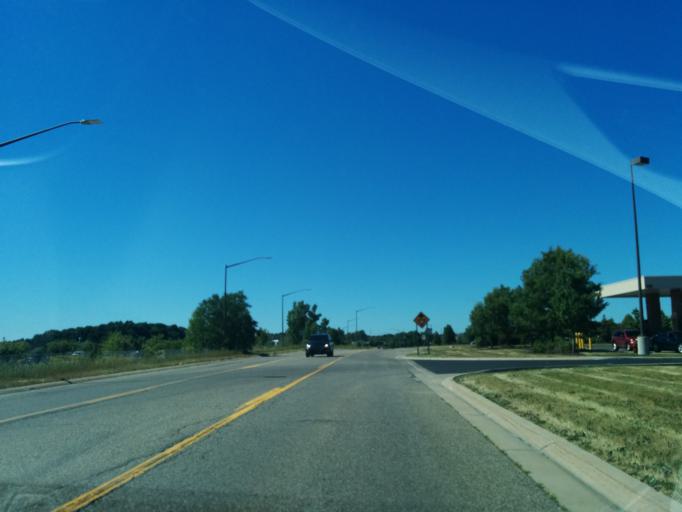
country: US
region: Michigan
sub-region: Oakland County
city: Walled Lake
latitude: 42.5340
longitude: -83.4473
